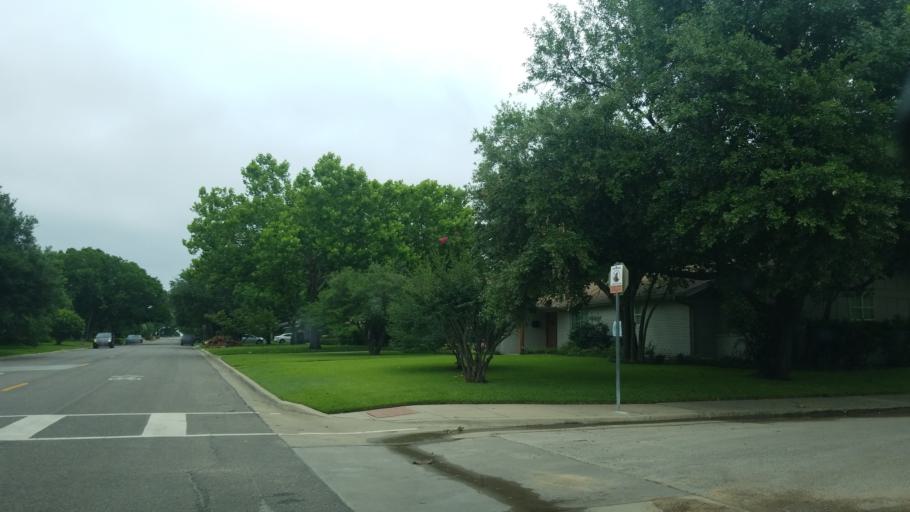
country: US
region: Texas
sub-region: Dallas County
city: Farmers Branch
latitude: 32.9023
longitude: -96.8607
